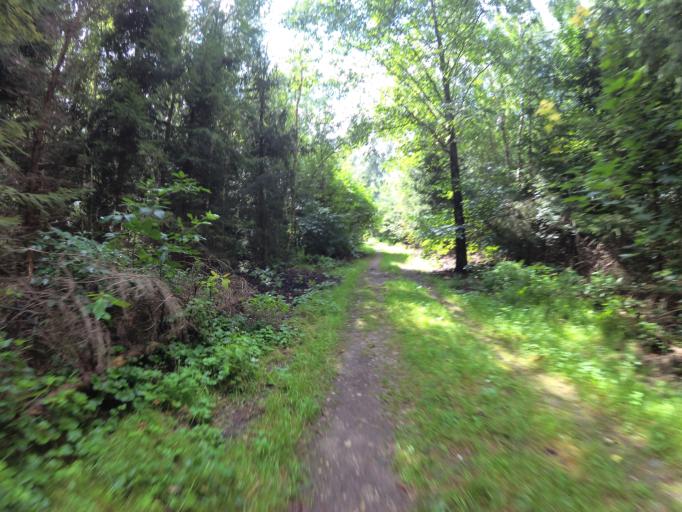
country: PL
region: Pomeranian Voivodeship
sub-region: Gdynia
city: Wielki Kack
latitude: 54.5040
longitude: 18.4491
